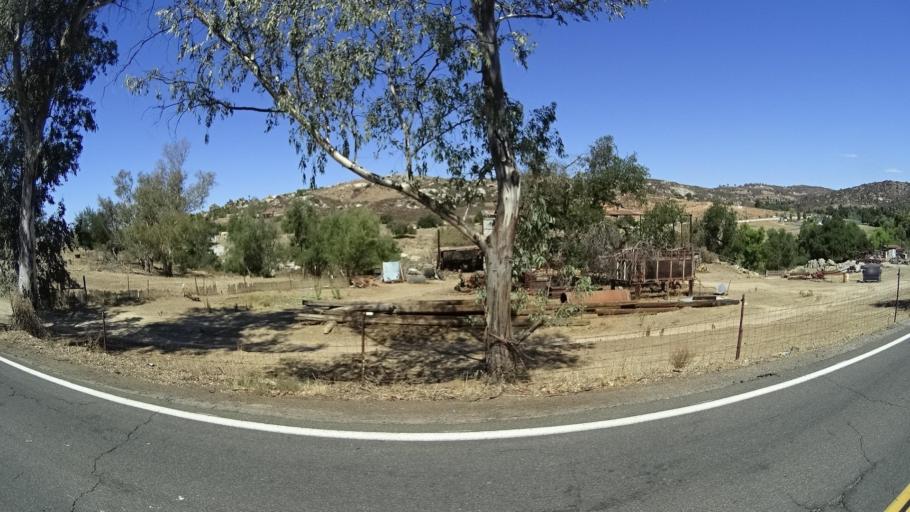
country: US
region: California
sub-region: San Diego County
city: Ramona
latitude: 33.0454
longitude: -116.8221
